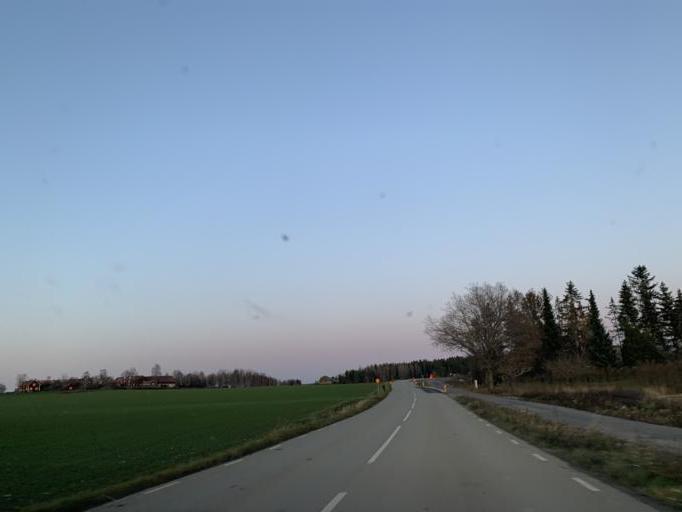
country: SE
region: OErebro
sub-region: Lindesbergs Kommun
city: Frovi
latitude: 59.3127
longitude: 15.3703
